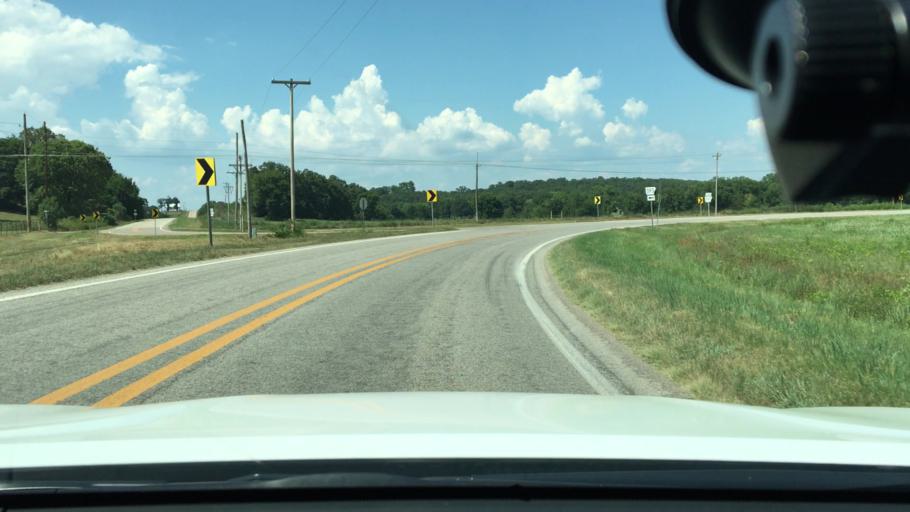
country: US
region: Arkansas
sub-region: Logan County
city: Paris
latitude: 35.3366
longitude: -93.6317
